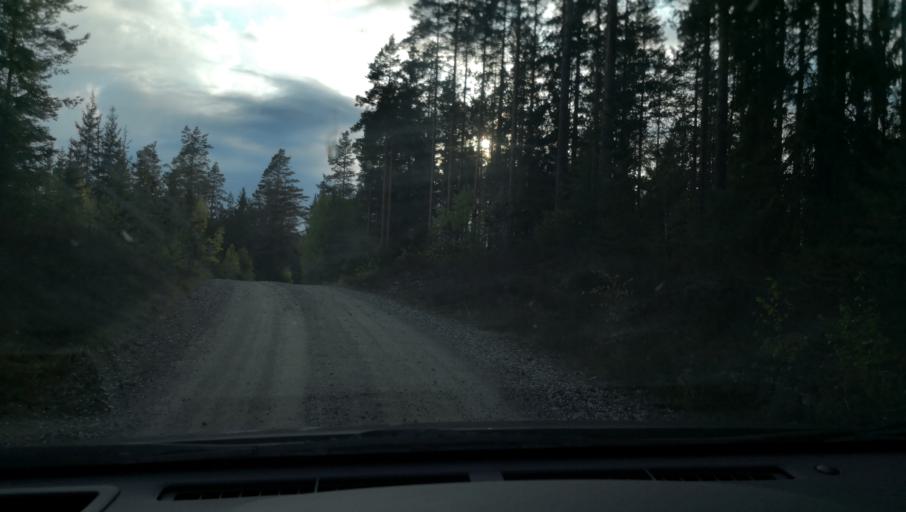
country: SE
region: Vaestmanland
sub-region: Skinnskattebergs Kommun
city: Skinnskatteberg
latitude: 59.7991
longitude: 15.4863
